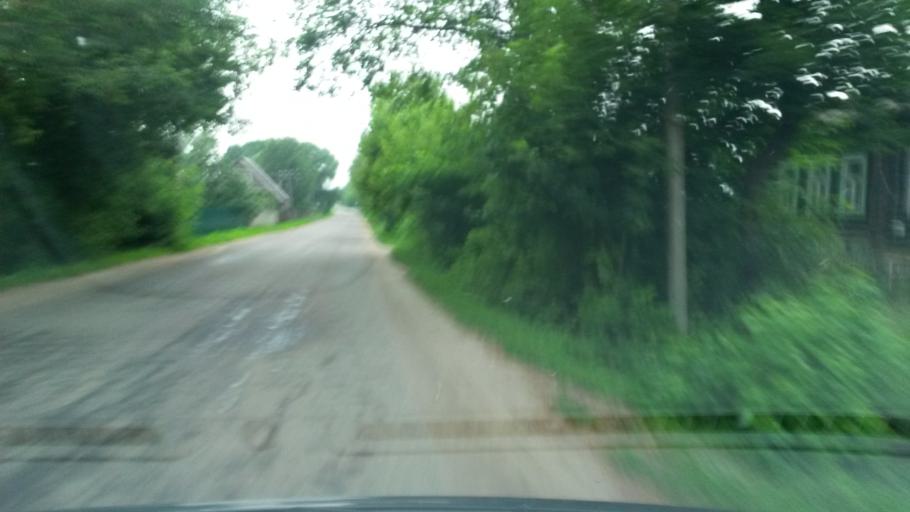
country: RU
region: Ivanovo
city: Pistsovo
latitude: 57.1784
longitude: 40.5270
